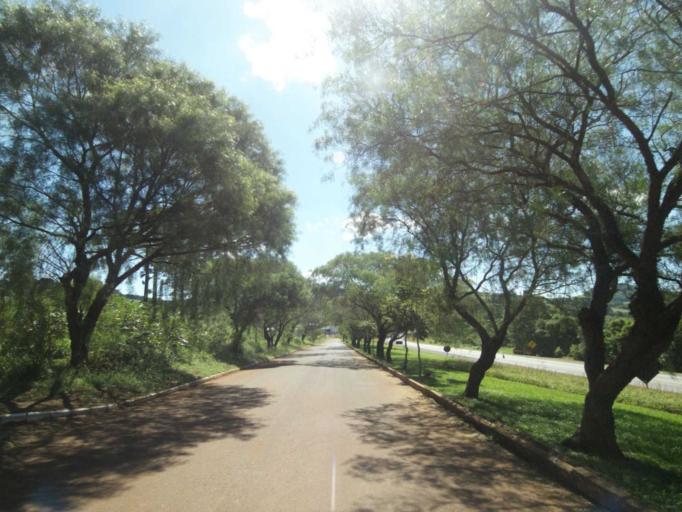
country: BR
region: Parana
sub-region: Laranjeiras Do Sul
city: Laranjeiras do Sul
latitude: -25.3791
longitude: -52.2061
